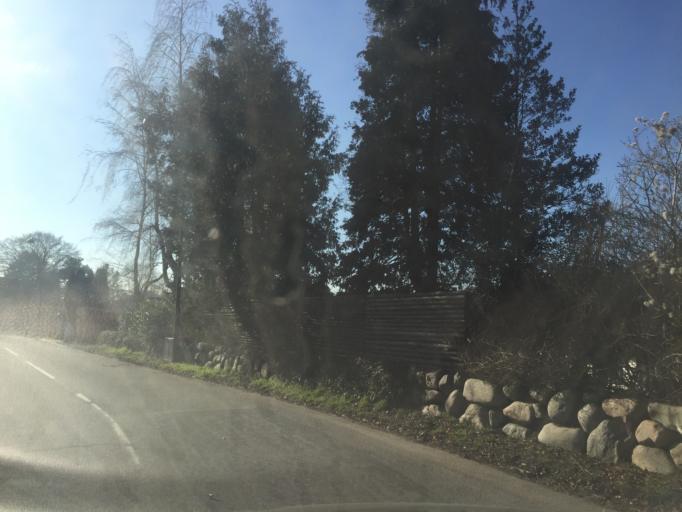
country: DK
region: Capital Region
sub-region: Rudersdal Kommune
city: Trorod
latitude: 55.8582
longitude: 12.5421
